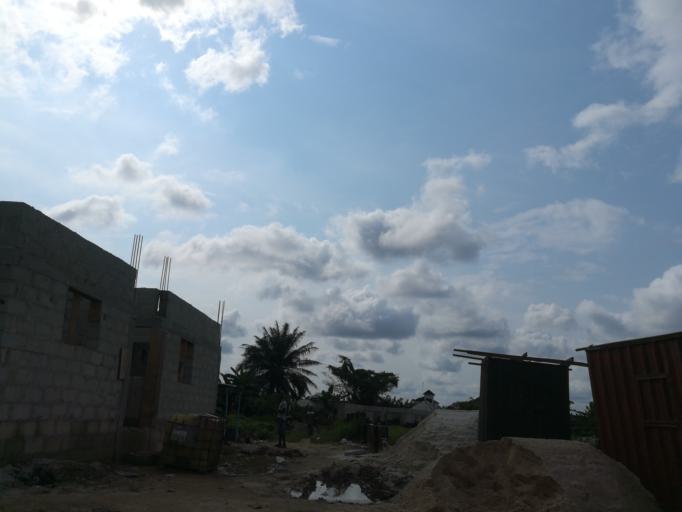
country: NG
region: Rivers
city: Okrika
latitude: 4.7622
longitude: 7.0937
